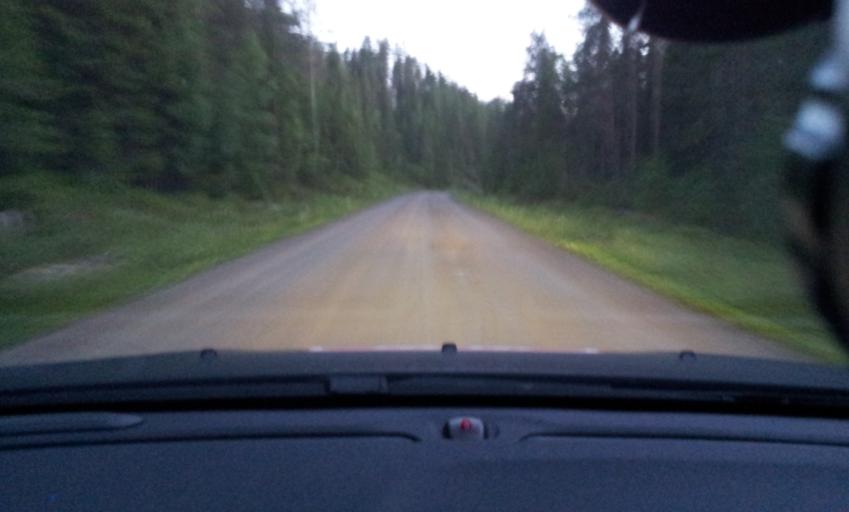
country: SE
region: Vaesternorrland
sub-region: Ange Kommun
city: Fransta
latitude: 62.7724
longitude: 15.9286
